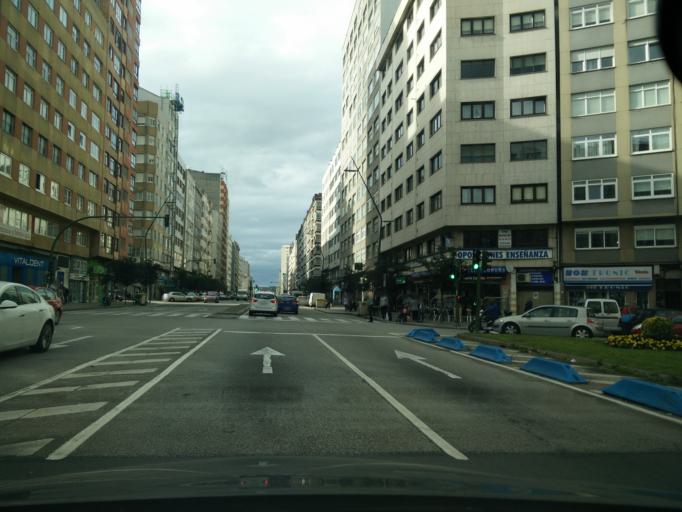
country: ES
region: Galicia
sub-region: Provincia da Coruna
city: A Coruna
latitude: 43.3590
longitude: -8.4200
